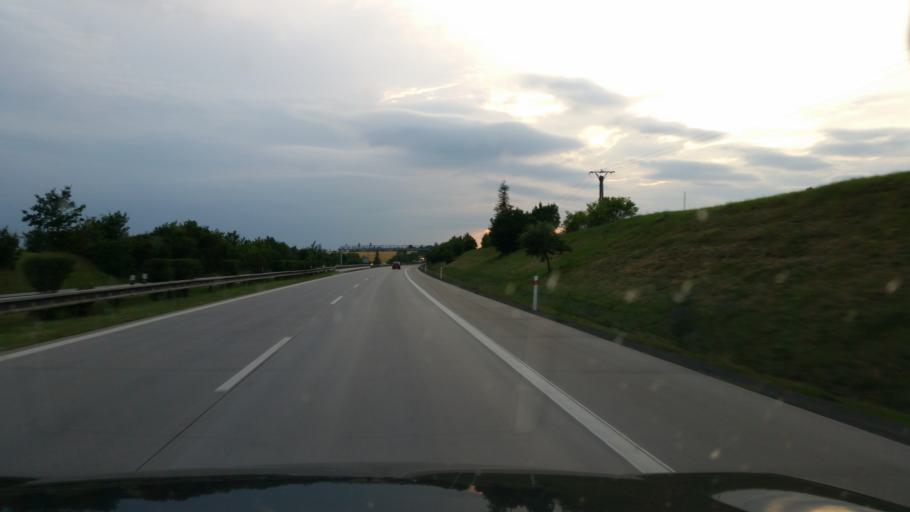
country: CZ
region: Olomoucky
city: Velky Ujezd
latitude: 49.5706
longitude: 17.4857
